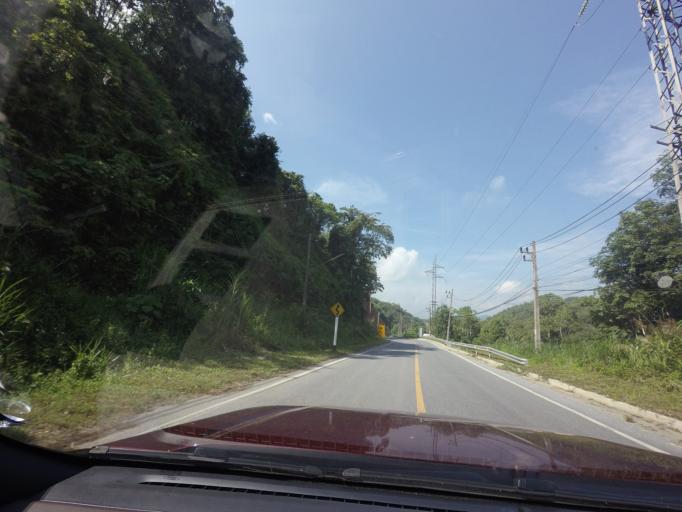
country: TH
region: Yala
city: Betong
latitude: 5.8993
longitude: 101.1461
